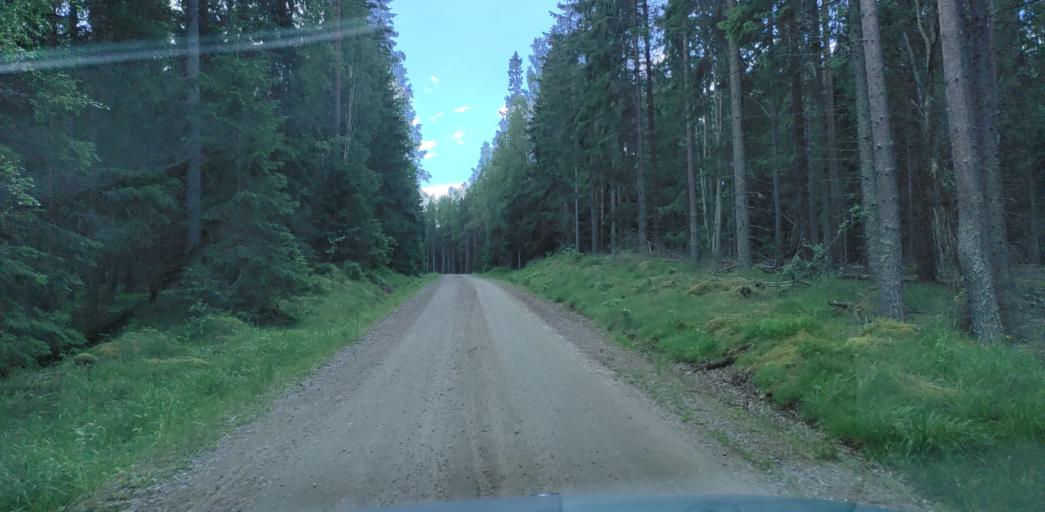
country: SE
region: Vaermland
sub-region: Hagfors Kommun
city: Ekshaerad
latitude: 60.0551
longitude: 13.3102
